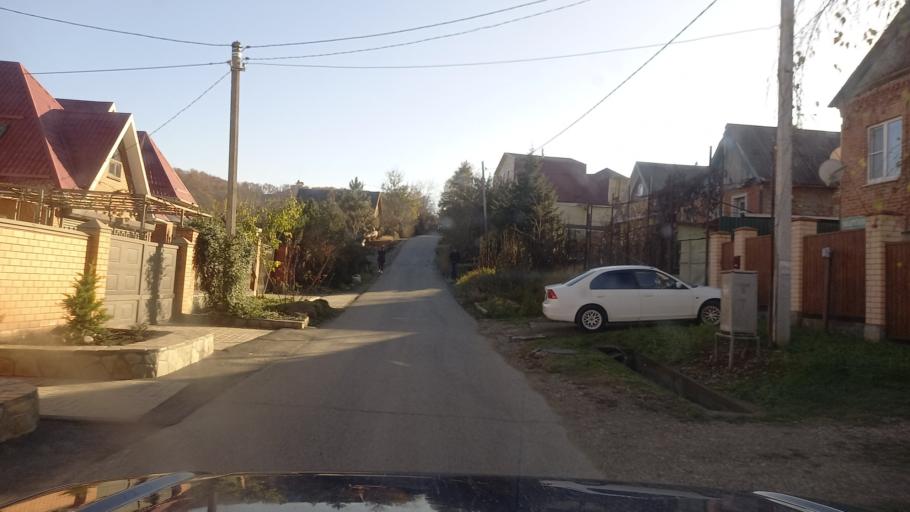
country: RU
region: Krasnodarskiy
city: Goryachiy Klyuch
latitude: 44.6243
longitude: 39.1064
